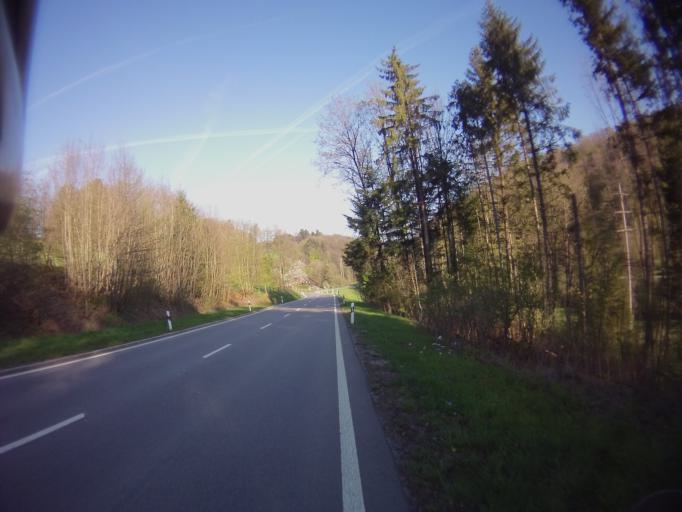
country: CH
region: Zurich
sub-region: Bezirk Dietikon
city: Birmensdorf
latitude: 47.3439
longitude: 8.4504
